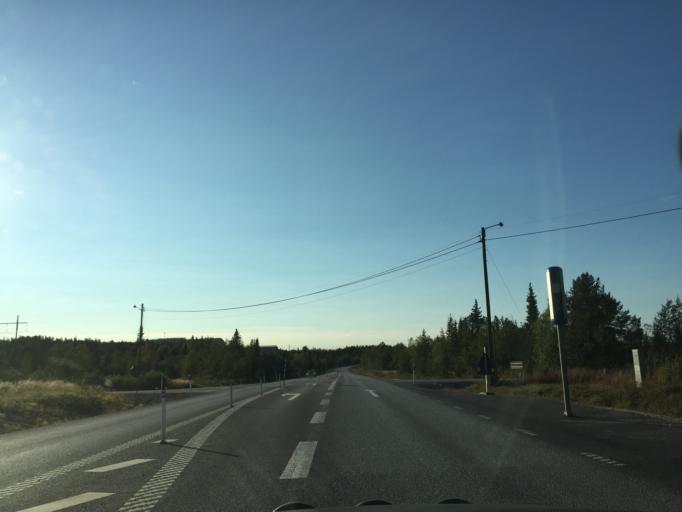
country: SE
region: Norrbotten
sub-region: Gallivare Kommun
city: Malmberget
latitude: 67.6451
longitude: 21.0424
